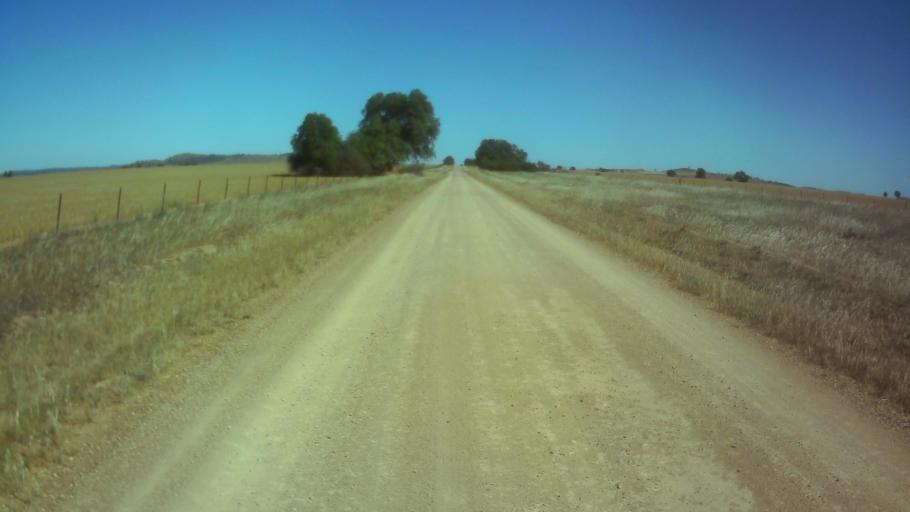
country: AU
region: New South Wales
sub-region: Weddin
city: Grenfell
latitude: -33.9886
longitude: 148.3366
